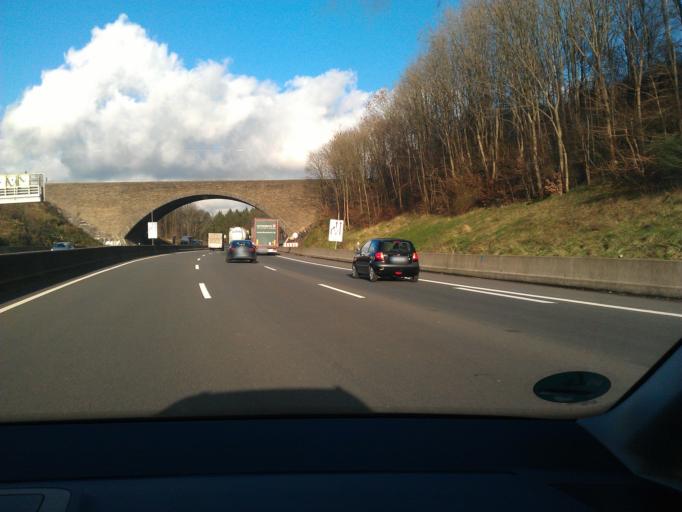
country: DE
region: North Rhine-Westphalia
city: Wermelskirchen
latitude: 51.1365
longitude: 7.1901
